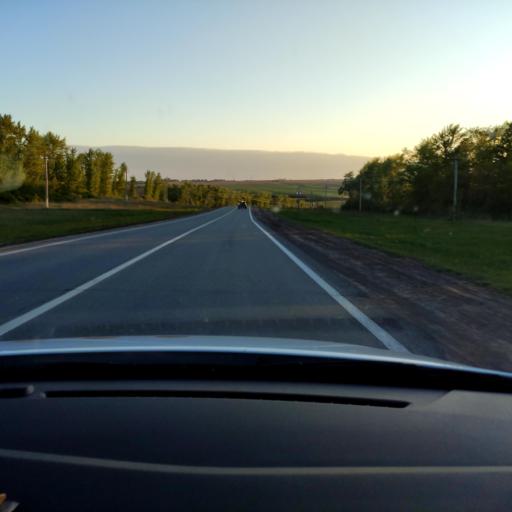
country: RU
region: Tatarstan
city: Pestretsy
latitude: 55.8182
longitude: 49.5513
